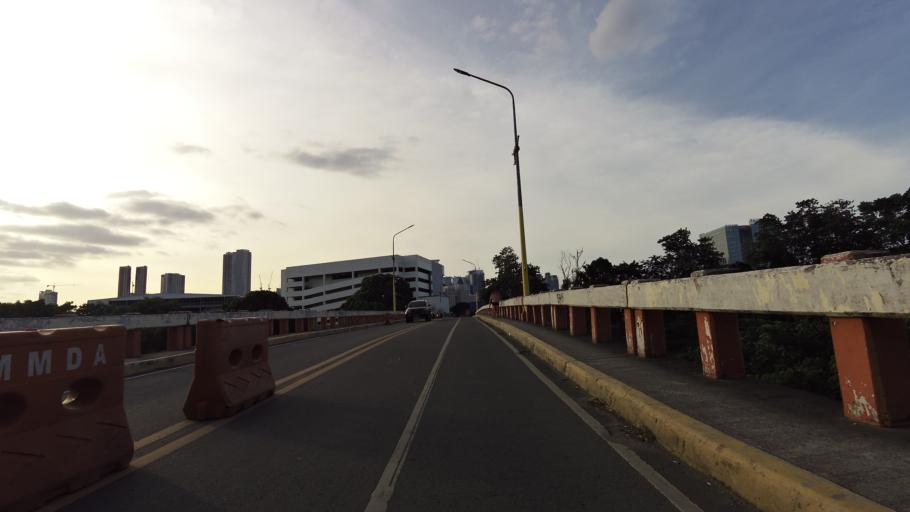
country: PH
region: Metro Manila
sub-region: Pasig
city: Pasig City
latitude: 14.5744
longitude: 121.0770
